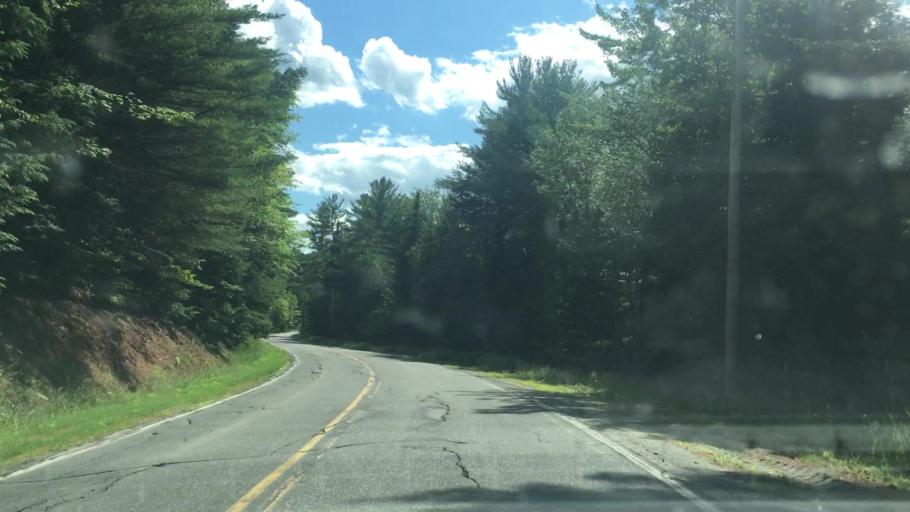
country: US
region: Maine
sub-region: Franklin County
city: Farmington
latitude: 44.7065
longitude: -70.1002
